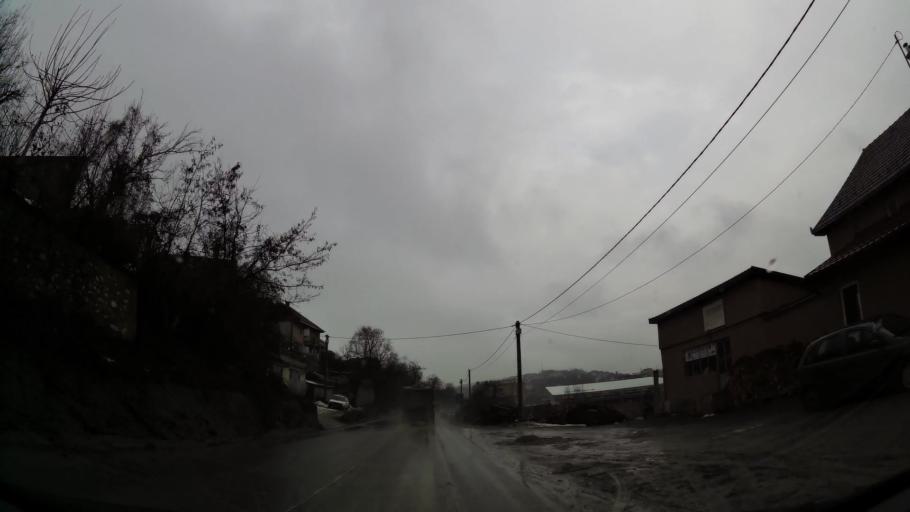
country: XK
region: Ferizaj
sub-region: Komuna e Kacanikut
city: Kacanik
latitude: 42.2259
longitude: 21.2544
